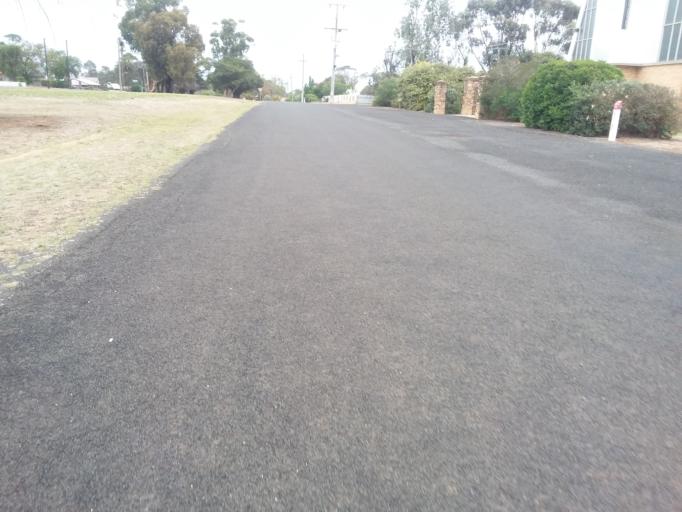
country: AU
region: Victoria
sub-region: Horsham
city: Horsham
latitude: -36.7429
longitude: 141.9382
